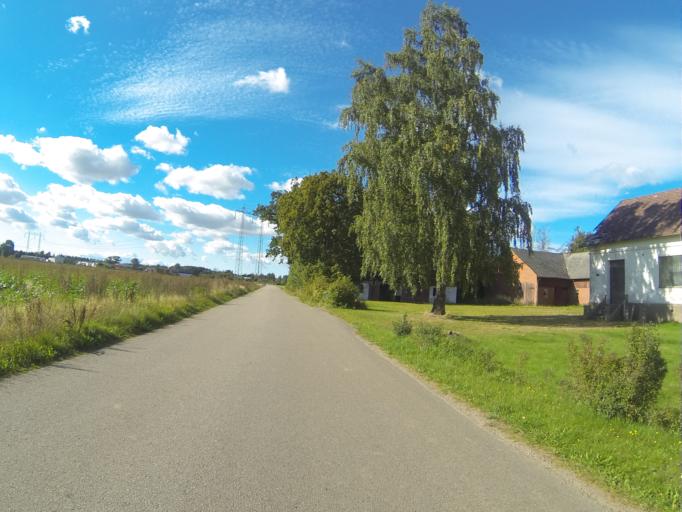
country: SE
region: Skane
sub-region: Lunds Kommun
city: Genarp
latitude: 55.7201
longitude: 13.3760
